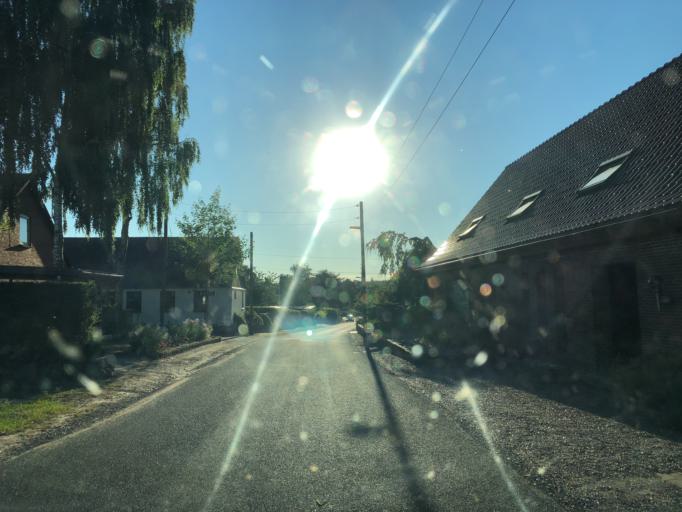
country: DK
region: Central Jutland
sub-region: Horsens Kommune
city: Horsens
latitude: 55.8952
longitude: 9.8458
